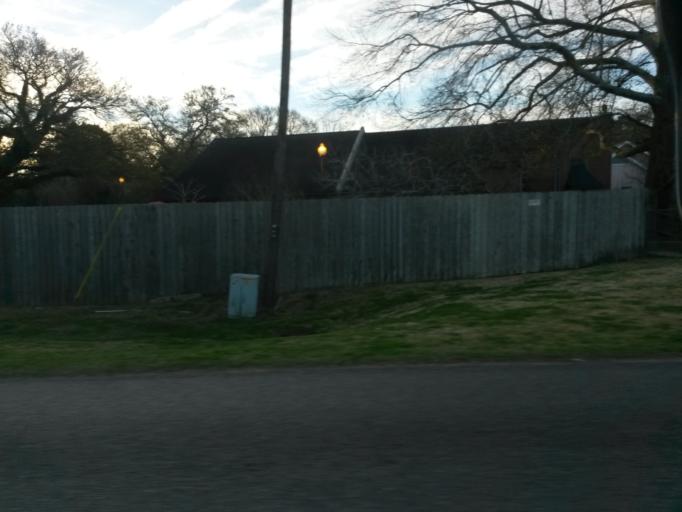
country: US
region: Louisiana
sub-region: Lafayette Parish
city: Lafayette
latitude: 30.2317
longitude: -92.0396
